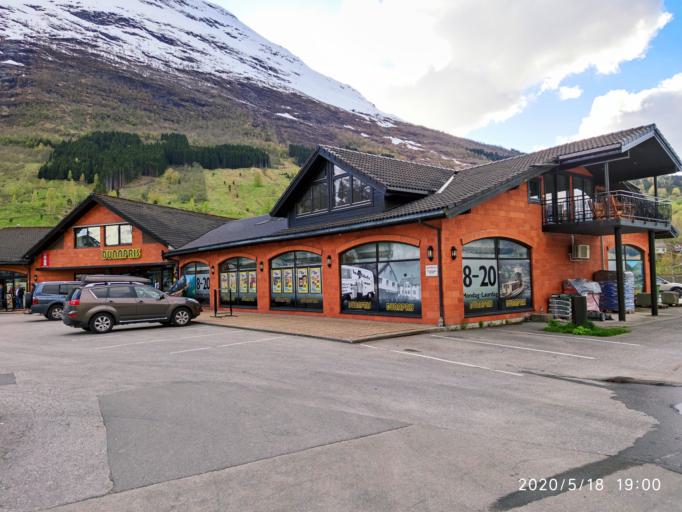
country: NO
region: Sogn og Fjordane
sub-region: Stryn
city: Stryn
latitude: 61.8353
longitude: 6.8055
